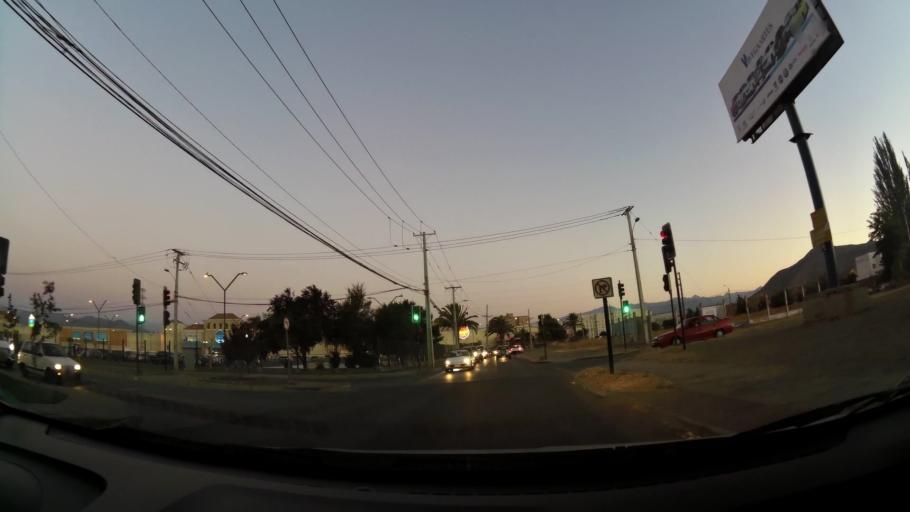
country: CL
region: O'Higgins
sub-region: Provincia de Cachapoal
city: Rancagua
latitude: -34.1855
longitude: -70.7276
